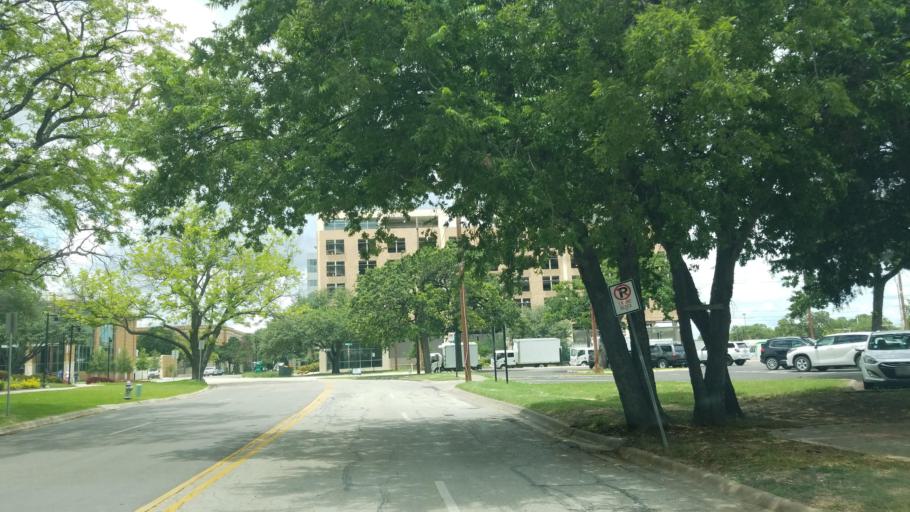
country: US
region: Texas
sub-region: Denton County
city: Denton
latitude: 33.2075
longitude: -97.1460
